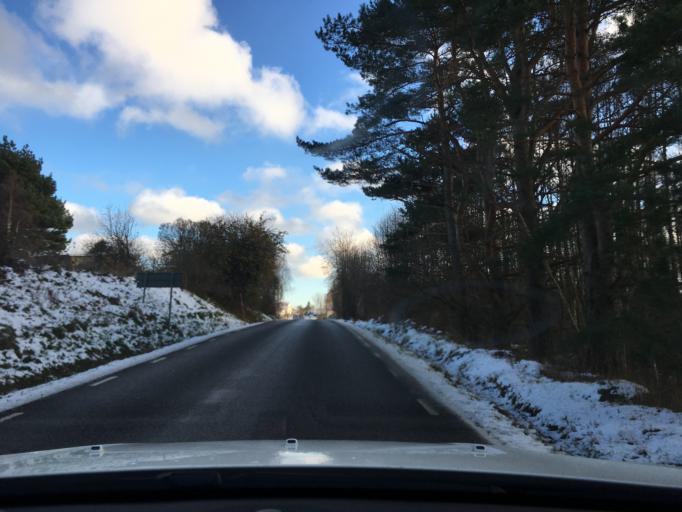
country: SE
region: Vaestra Goetaland
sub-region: Tjorns Kommun
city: Myggenas
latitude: 58.0523
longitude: 11.7050
